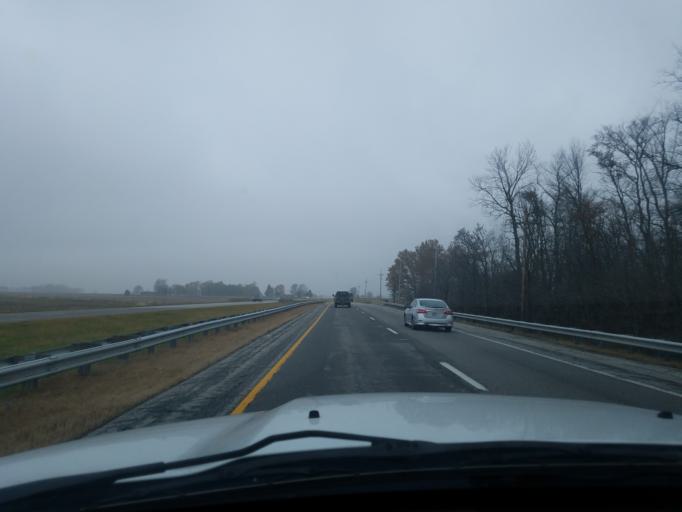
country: US
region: Indiana
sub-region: Howard County
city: Indian Heights
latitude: 40.3620
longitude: -86.1271
